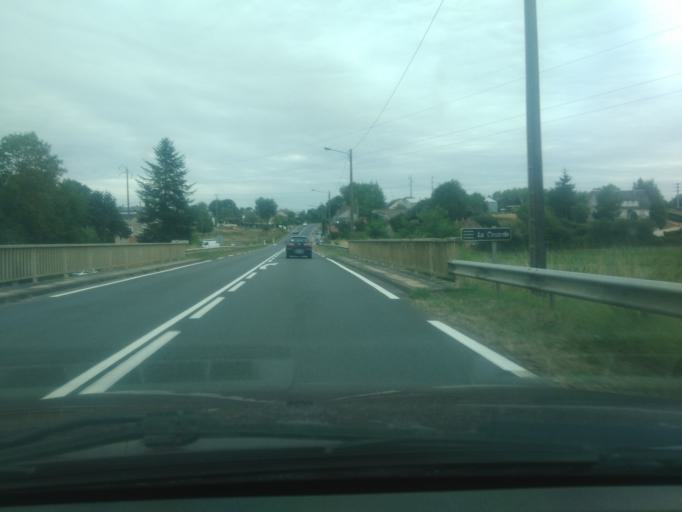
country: FR
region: Centre
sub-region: Departement de l'Indre
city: La Chatre
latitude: 46.5769
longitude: 1.9638
